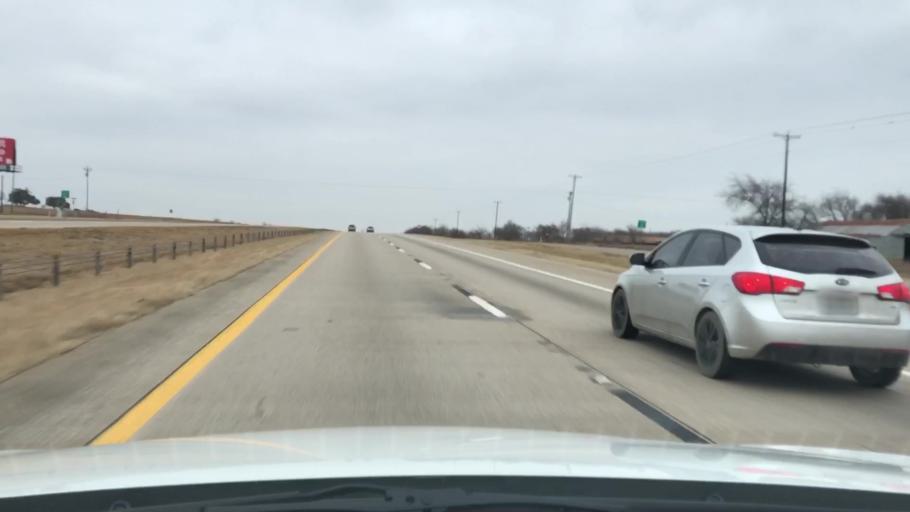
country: US
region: Texas
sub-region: Cooke County
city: Gainesville
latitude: 33.5628
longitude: -97.1660
